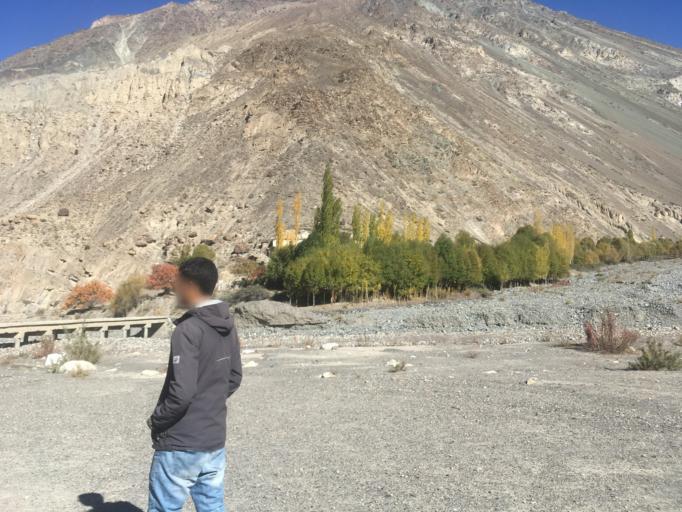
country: PK
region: Gilgit-Baltistan
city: Skardu
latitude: 35.1937
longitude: 75.6214
